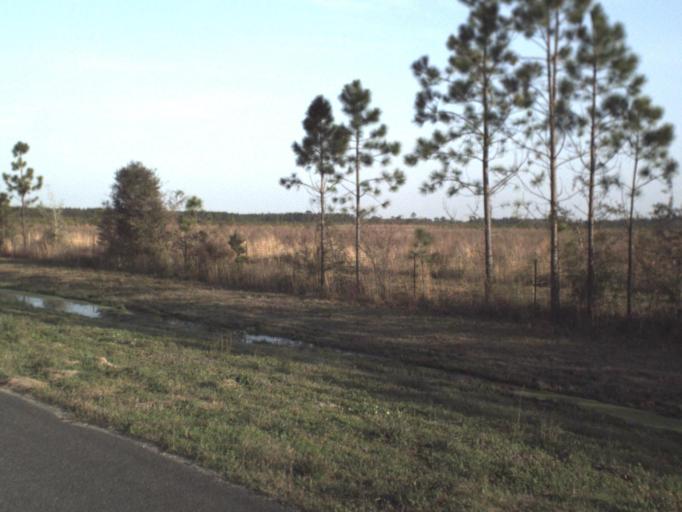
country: US
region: Florida
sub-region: Bay County
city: Lynn Haven
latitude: 30.4390
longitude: -85.7161
